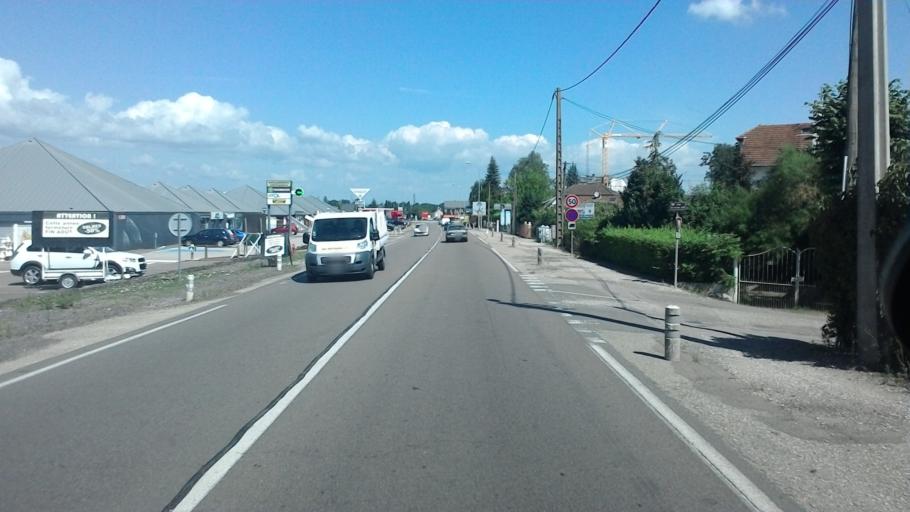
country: FR
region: Bourgogne
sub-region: Departement de Saone-et-Loire
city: Saint-Remy
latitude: 46.7515
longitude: 4.8486
